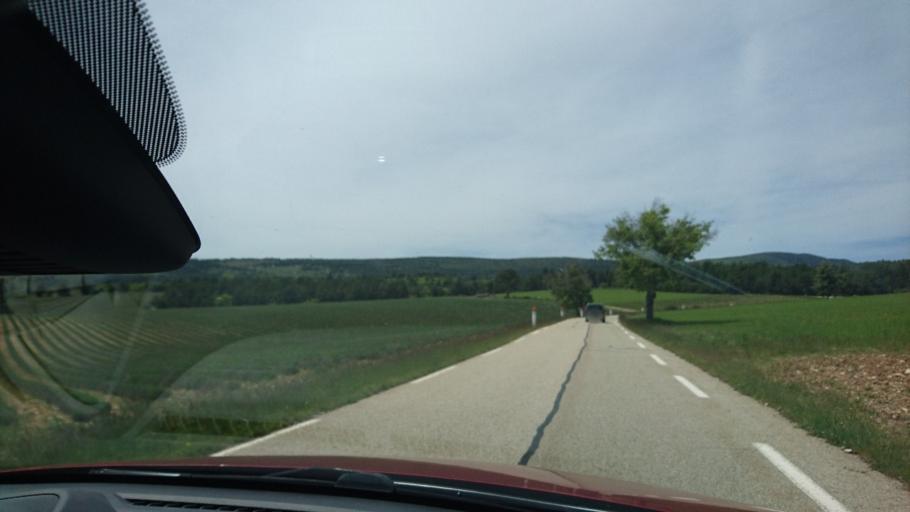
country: FR
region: Provence-Alpes-Cote d'Azur
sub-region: Departement du Vaucluse
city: Sault
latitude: 44.1153
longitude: 5.3882
